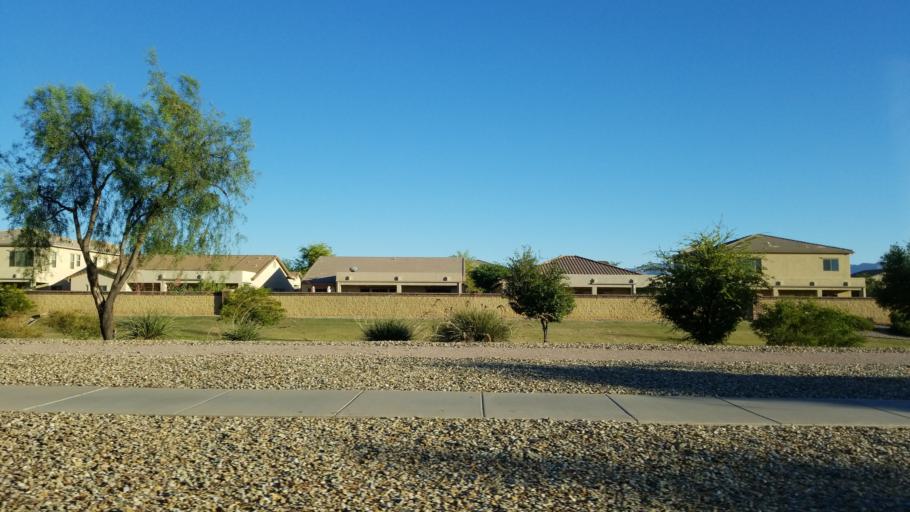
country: US
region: Arizona
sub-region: Maricopa County
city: Laveen
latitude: 33.3774
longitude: -112.1735
